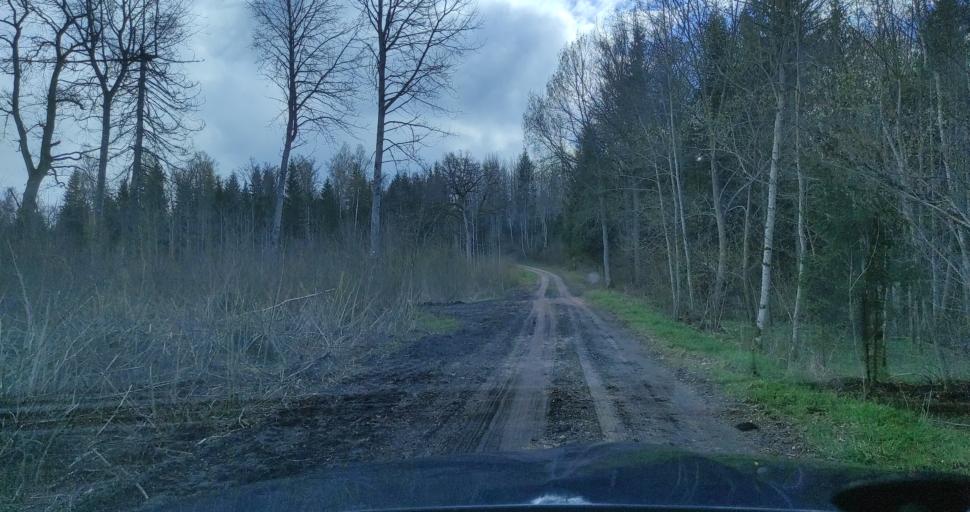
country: LV
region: Kuldigas Rajons
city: Kuldiga
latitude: 56.8643
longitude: 21.8292
